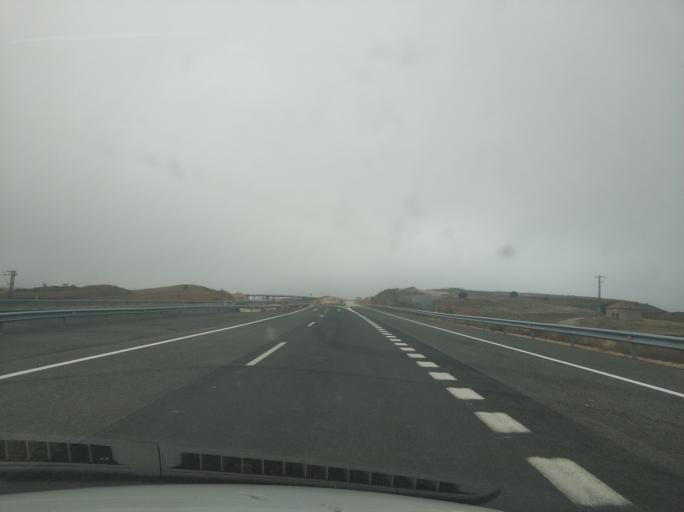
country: ES
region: Castille and Leon
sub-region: Provincia de Soria
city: Adradas
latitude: 41.3530
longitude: -2.4787
